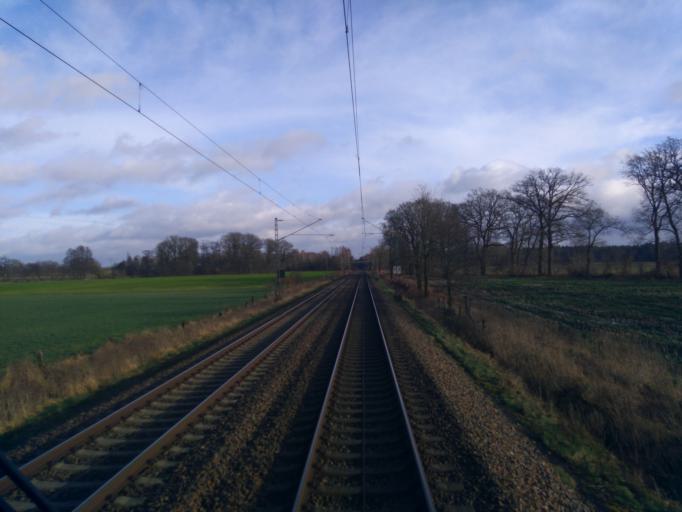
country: DE
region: Lower Saxony
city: Hassendorf
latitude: 53.1023
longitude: 9.2984
